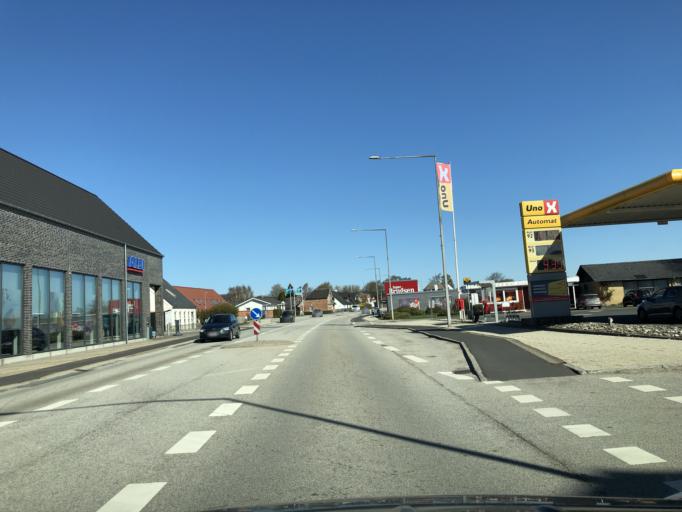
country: DK
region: North Denmark
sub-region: Rebild Kommune
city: Stovring
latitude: 56.8926
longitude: 9.8370
